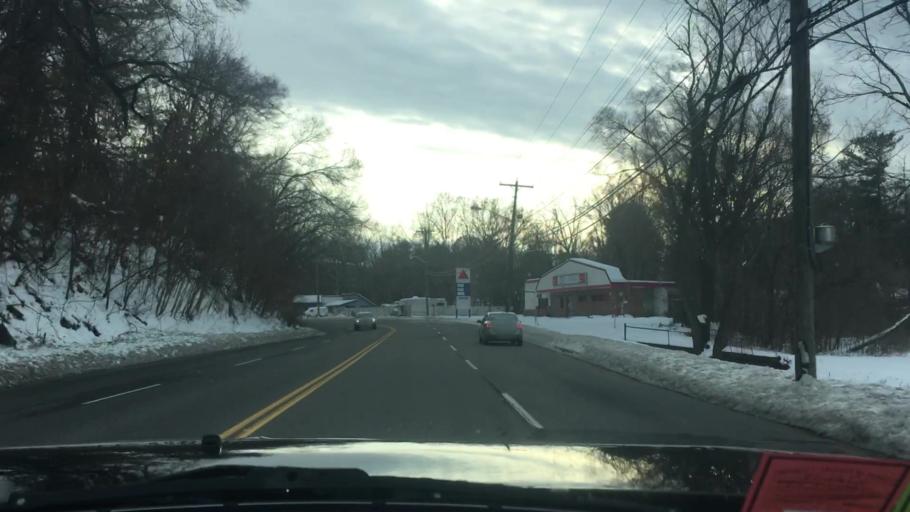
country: US
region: Virginia
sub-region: Pulaski County
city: Pulaski
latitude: 37.0550
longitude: -80.7735
